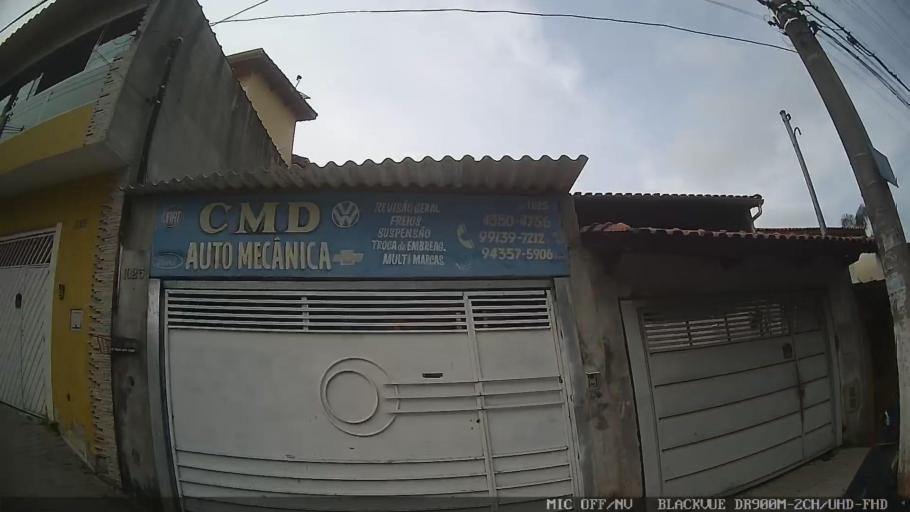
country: BR
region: Sao Paulo
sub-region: Poa
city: Poa
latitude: -23.5201
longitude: -46.3534
